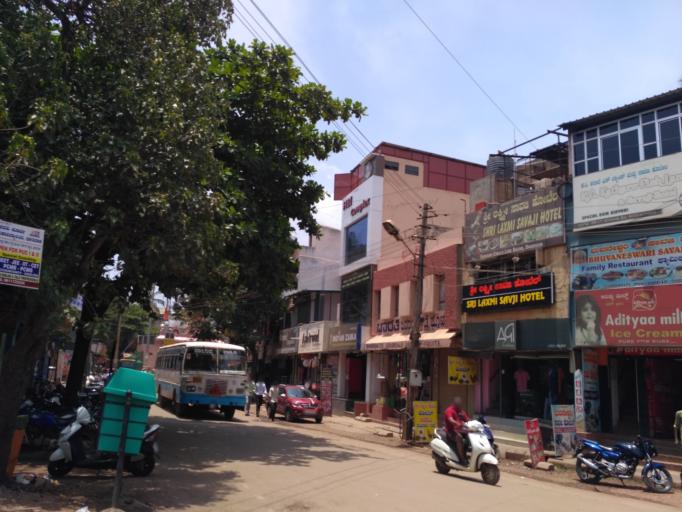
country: IN
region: Karnataka
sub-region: Dharwad
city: Hubli
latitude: 15.4546
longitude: 75.0100
